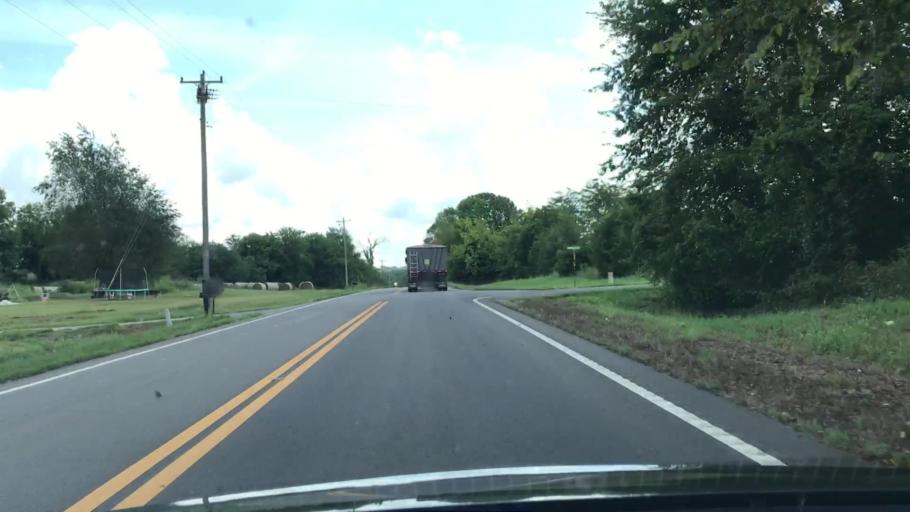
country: US
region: Tennessee
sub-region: Robertson County
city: Springfield
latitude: 36.6344
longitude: -86.9710
